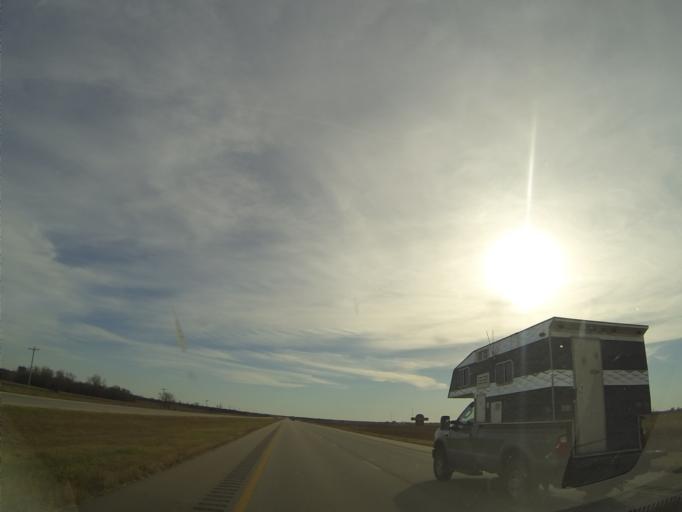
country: US
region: Kansas
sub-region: Ottawa County
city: Minneapolis
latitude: 39.1555
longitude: -97.6687
